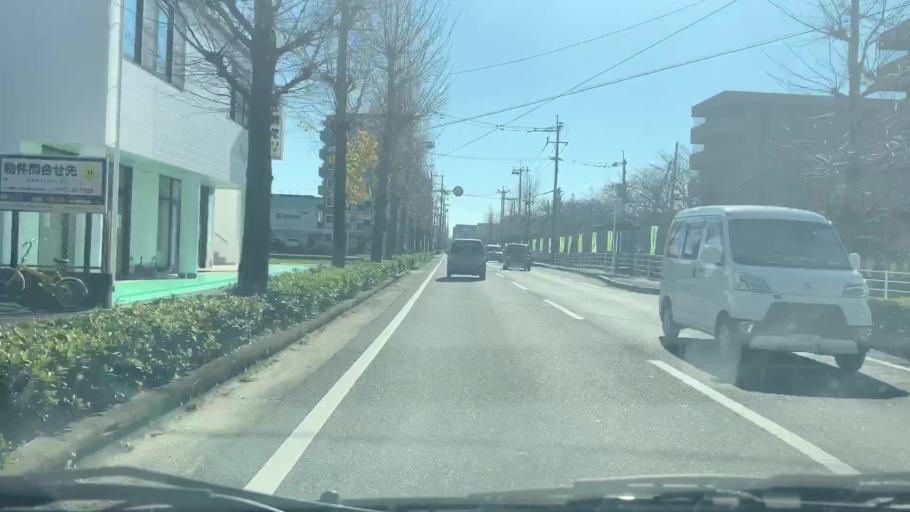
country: JP
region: Saga Prefecture
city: Saga-shi
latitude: 33.2871
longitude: 130.2682
